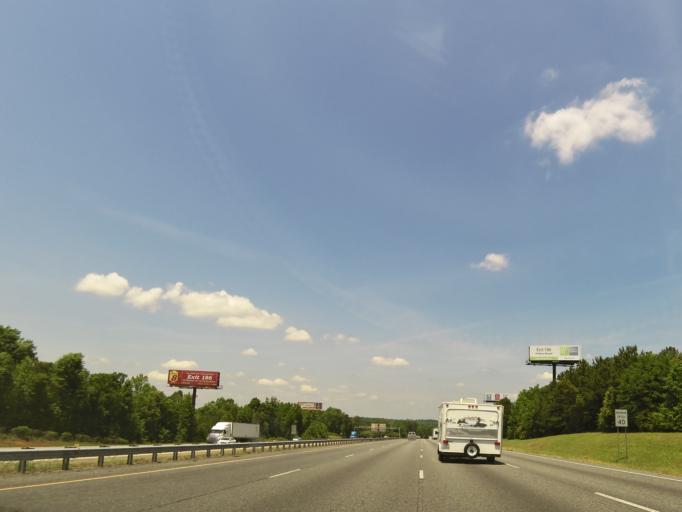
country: US
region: Georgia
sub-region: Monroe County
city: Forsyth
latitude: 32.9678
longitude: -83.8222
